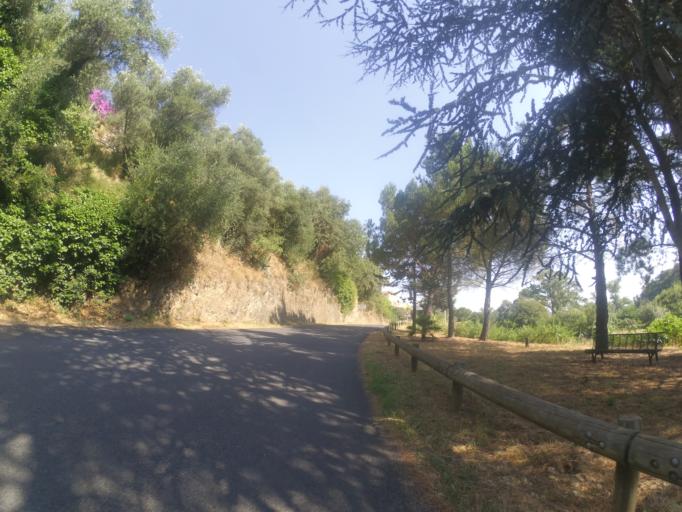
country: FR
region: Languedoc-Roussillon
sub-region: Departement des Pyrenees-Orientales
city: Ille-sur-Tet
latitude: 42.6504
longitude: 2.6227
